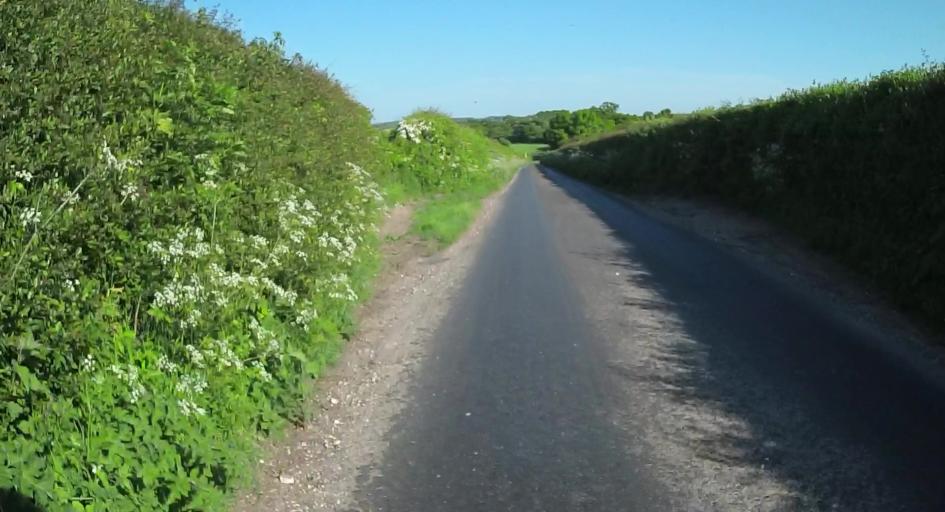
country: GB
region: England
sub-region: Hampshire
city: Overton
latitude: 51.1669
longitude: -1.1900
